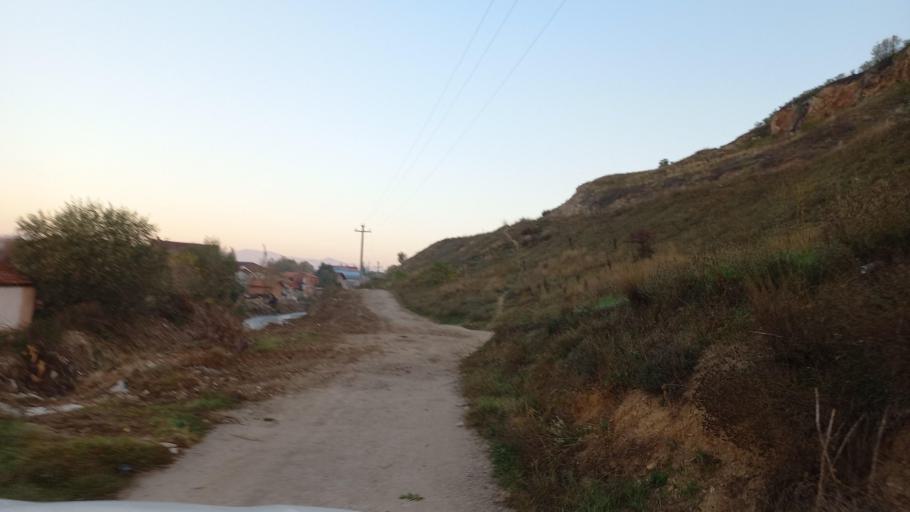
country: MK
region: Kumanovo
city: Kumanovo
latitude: 42.1402
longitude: 21.7254
